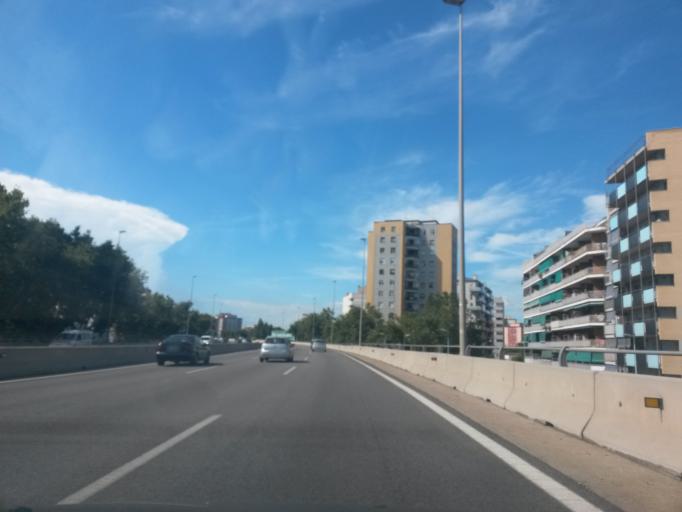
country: ES
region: Catalonia
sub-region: Provincia de Barcelona
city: Llefia
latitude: 41.4387
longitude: 2.2264
